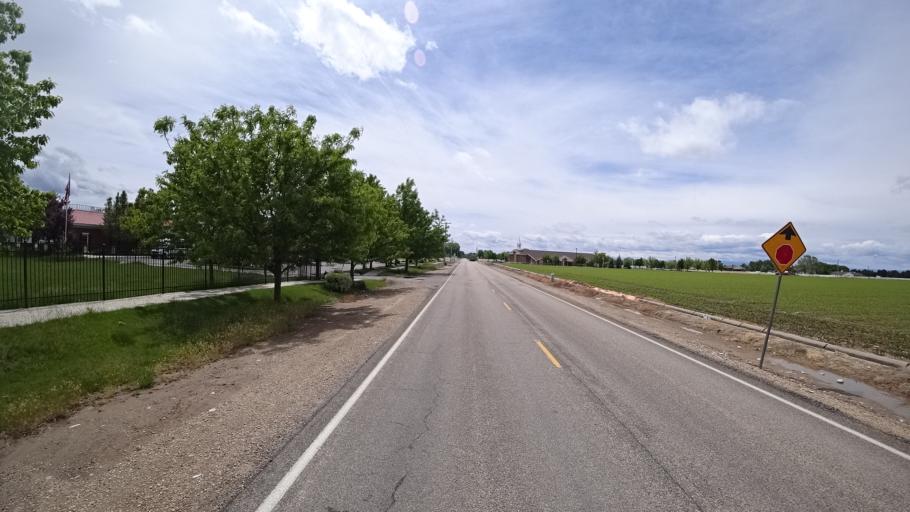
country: US
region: Idaho
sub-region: Ada County
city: Eagle
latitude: 43.7079
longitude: -116.4036
